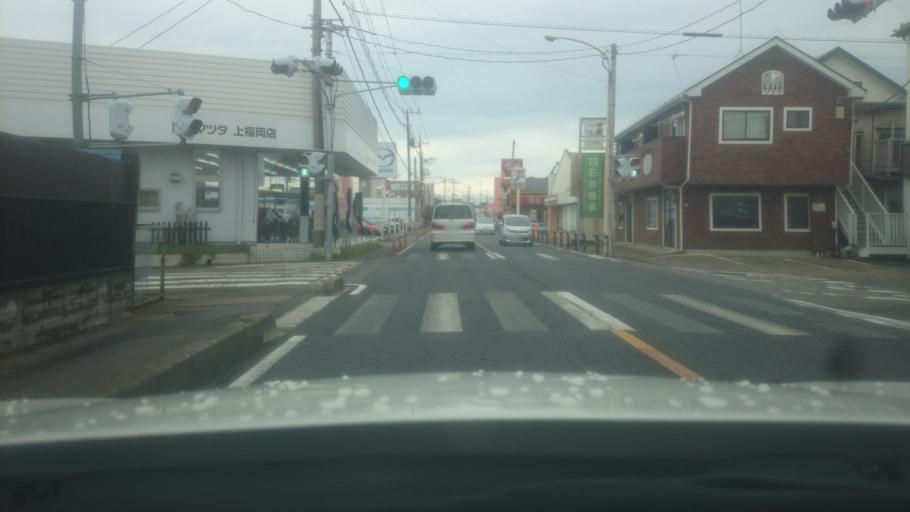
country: JP
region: Saitama
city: Kamifukuoka
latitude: 35.8768
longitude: 139.5004
